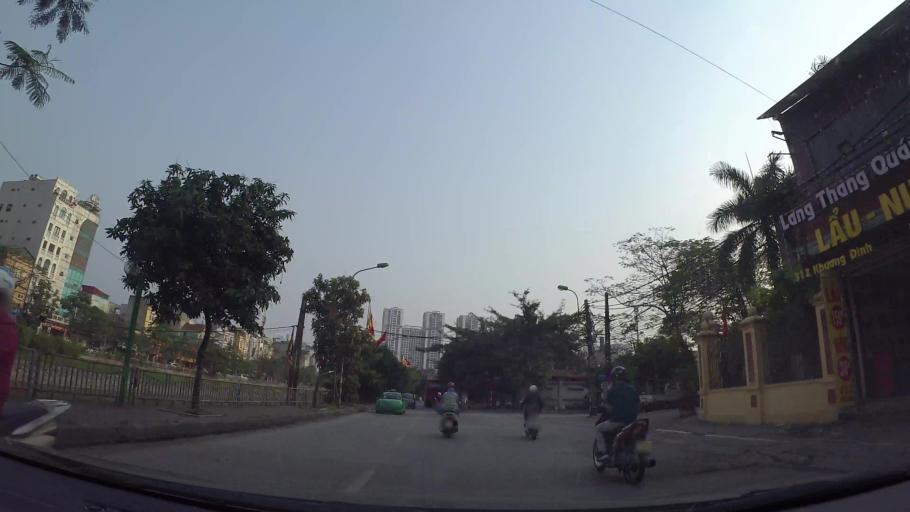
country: VN
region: Ha Noi
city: Thanh Xuan
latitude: 20.9906
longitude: 105.8132
